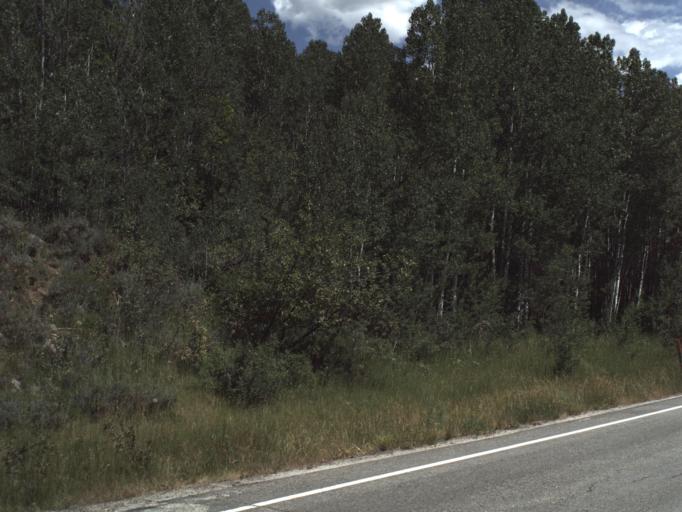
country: US
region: Utah
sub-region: Weber County
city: Wolf Creek
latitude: 41.3187
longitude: -111.6158
